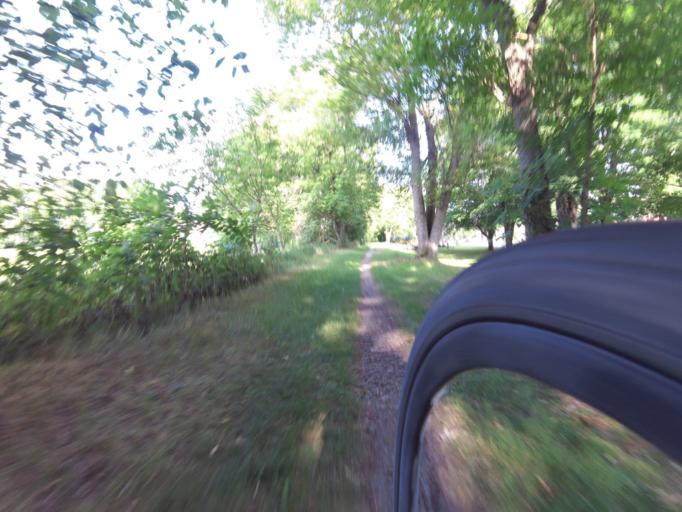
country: CA
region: Ontario
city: Kingston
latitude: 44.4232
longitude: -76.5731
